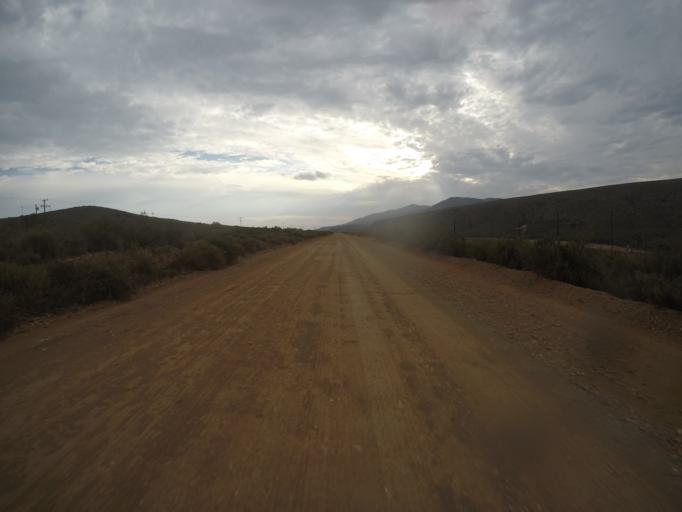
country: ZA
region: Eastern Cape
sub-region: Cacadu District Municipality
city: Willowmore
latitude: -33.4885
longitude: 23.5580
